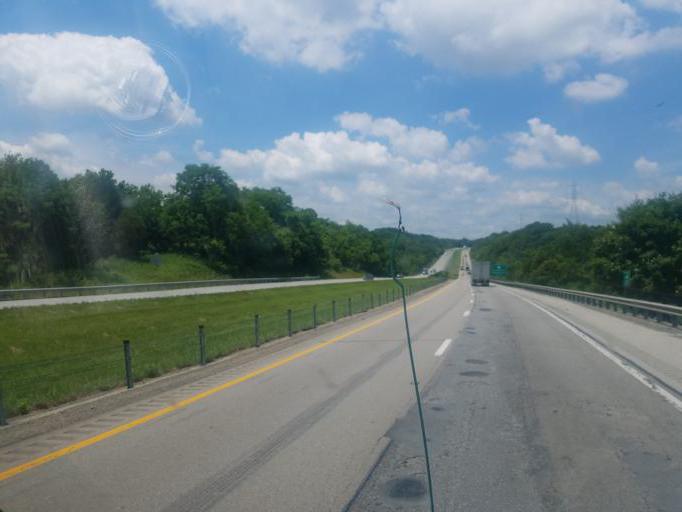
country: US
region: Indiana
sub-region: Switzerland County
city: Vevay
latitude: 38.6559
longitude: -85.0746
